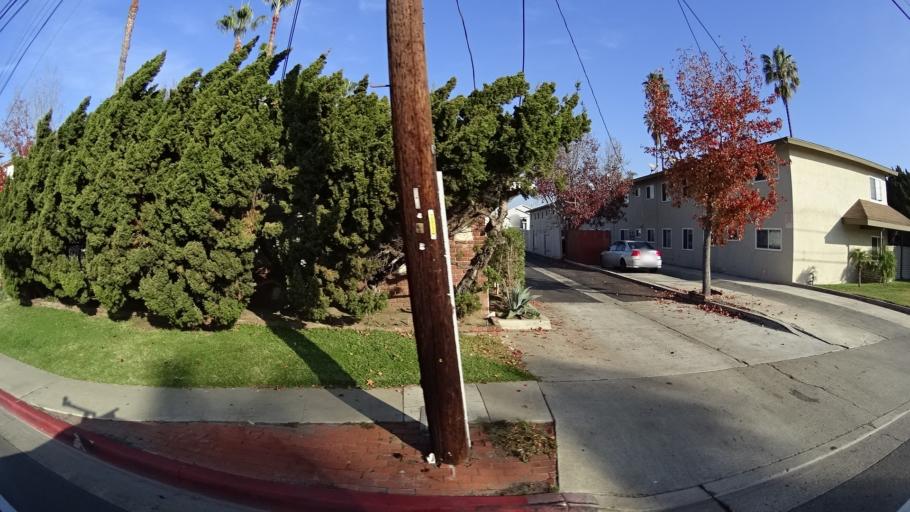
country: US
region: California
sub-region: Orange County
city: Costa Mesa
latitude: 33.6526
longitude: -117.9144
